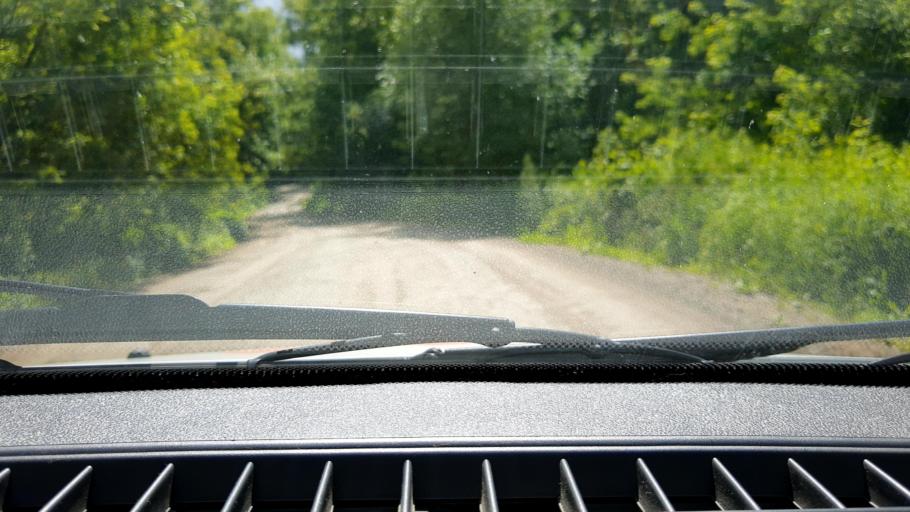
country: RU
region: Bashkortostan
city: Ufa
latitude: 54.6858
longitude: 56.0549
